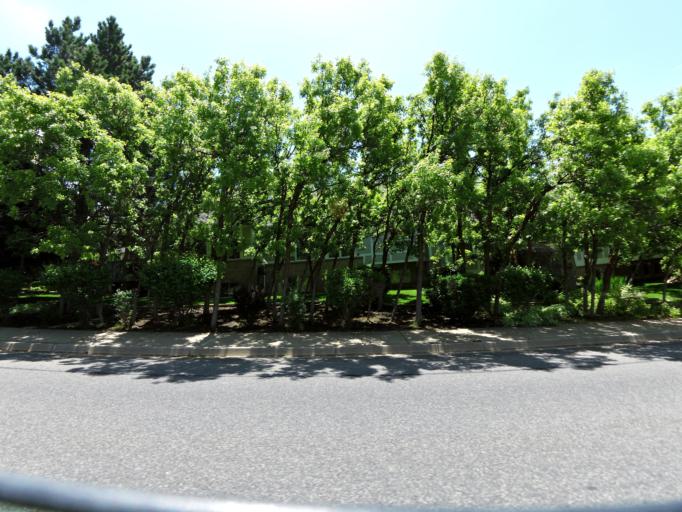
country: US
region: Utah
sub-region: Weber County
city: Uintah
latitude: 41.1788
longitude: -111.9346
